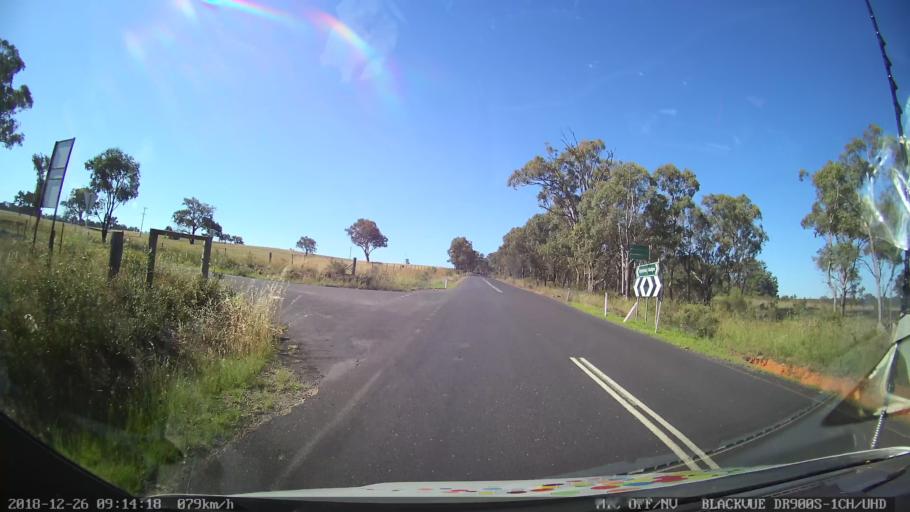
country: AU
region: New South Wales
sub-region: Mid-Western Regional
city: Kandos
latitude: -32.7770
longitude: 149.9789
